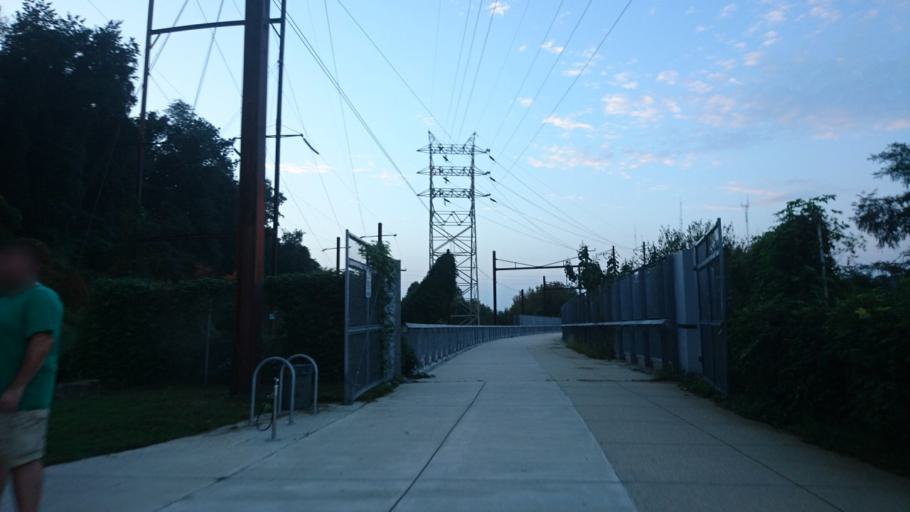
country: US
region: Pennsylvania
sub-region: Montgomery County
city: Bala-Cynwyd
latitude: 40.0230
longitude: -75.2252
